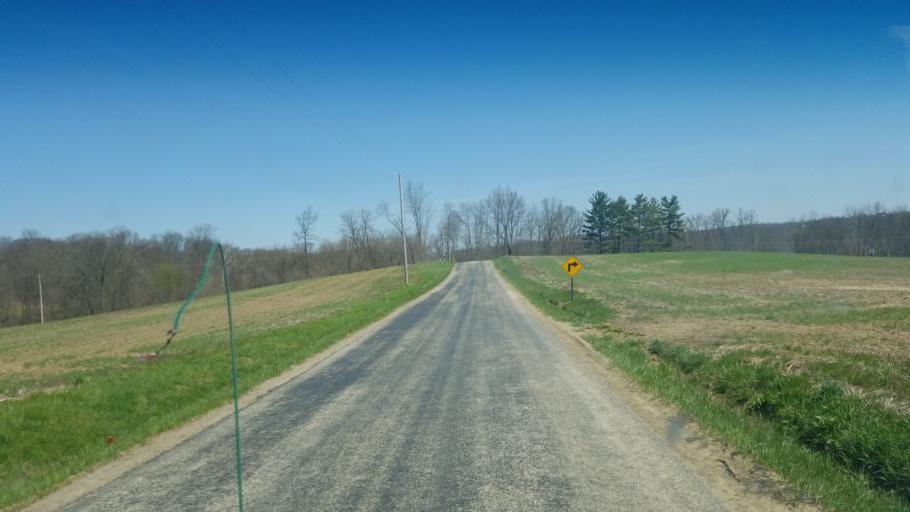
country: US
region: Ohio
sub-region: Richland County
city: Lincoln Heights
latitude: 40.8344
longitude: -82.4231
